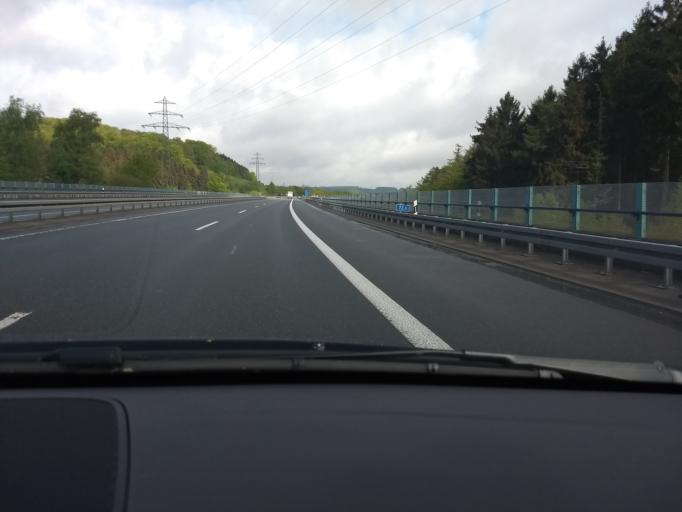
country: DE
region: North Rhine-Westphalia
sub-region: Regierungsbezirk Arnsberg
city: Arnsberg
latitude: 51.3701
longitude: 8.1585
